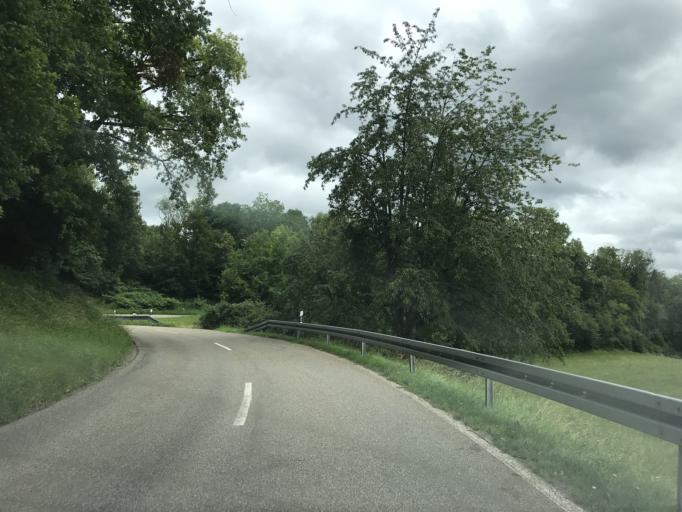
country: DE
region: Baden-Wuerttemberg
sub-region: Freiburg Region
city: Hasel
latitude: 47.6640
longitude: 7.8748
